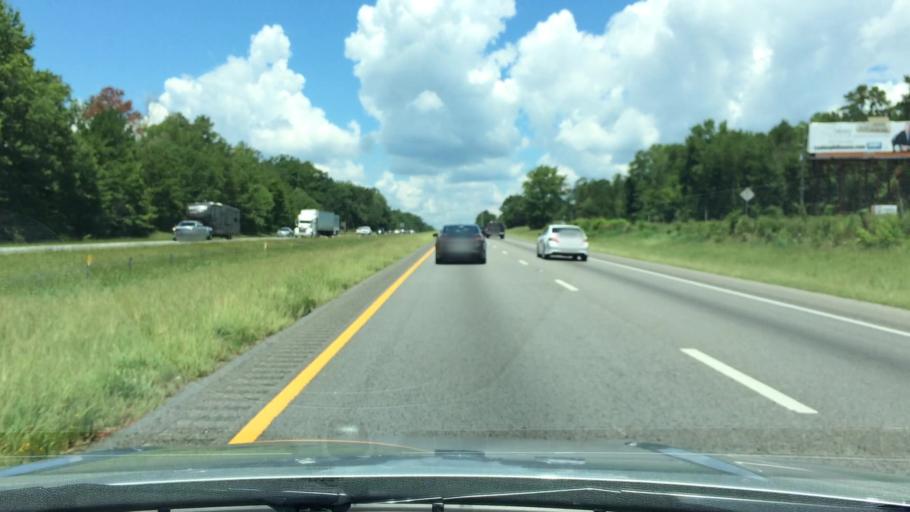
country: US
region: South Carolina
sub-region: Lexington County
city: Irmo
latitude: 34.1127
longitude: -81.1889
